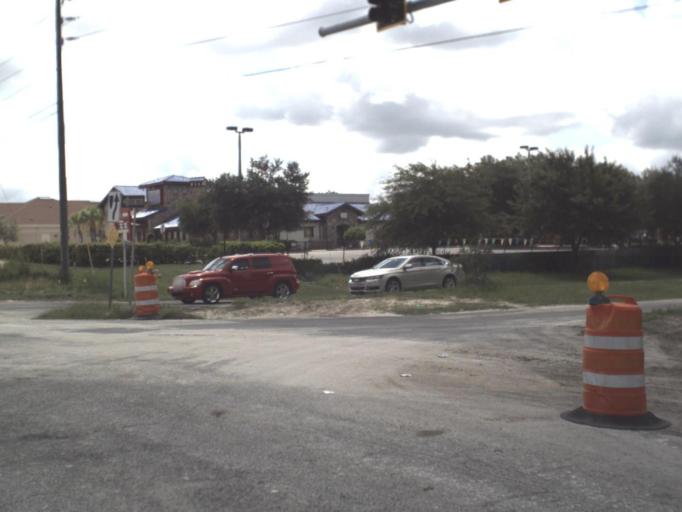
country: US
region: Florida
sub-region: Hernando County
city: High Point
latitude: 28.5334
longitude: -82.5280
